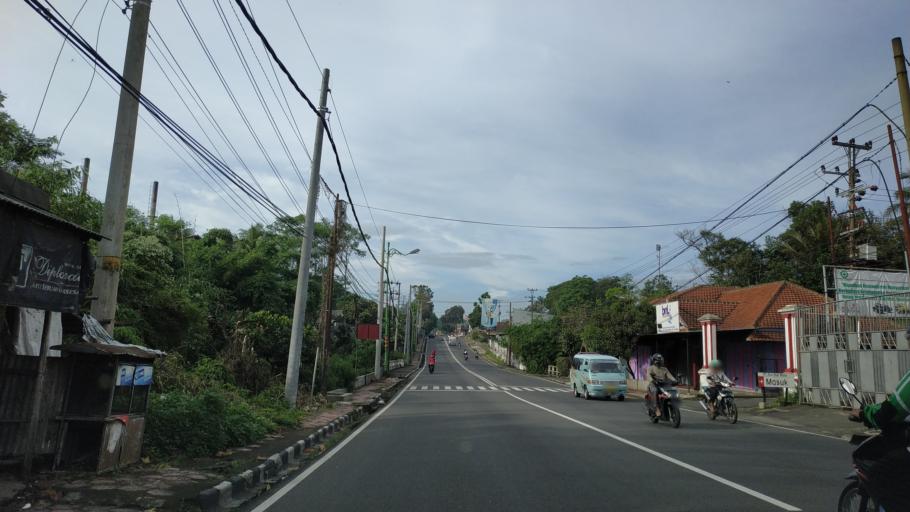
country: ID
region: Central Java
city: Salatiga
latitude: -7.3474
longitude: 110.5118
